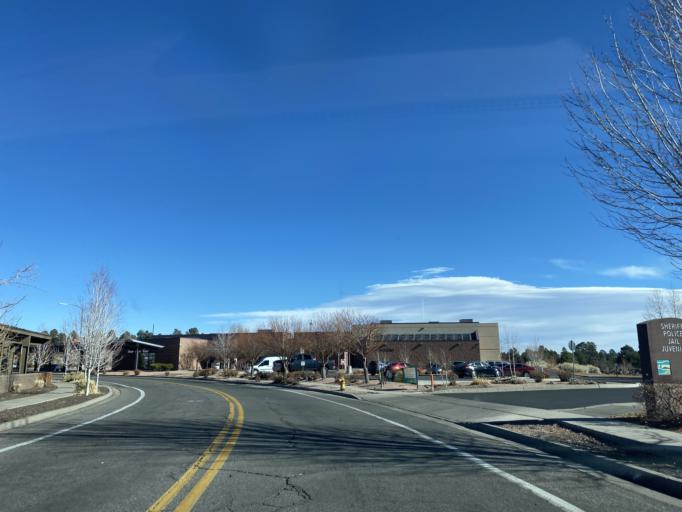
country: US
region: Arizona
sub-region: Coconino County
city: Flagstaff
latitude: 35.1888
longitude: -111.6419
